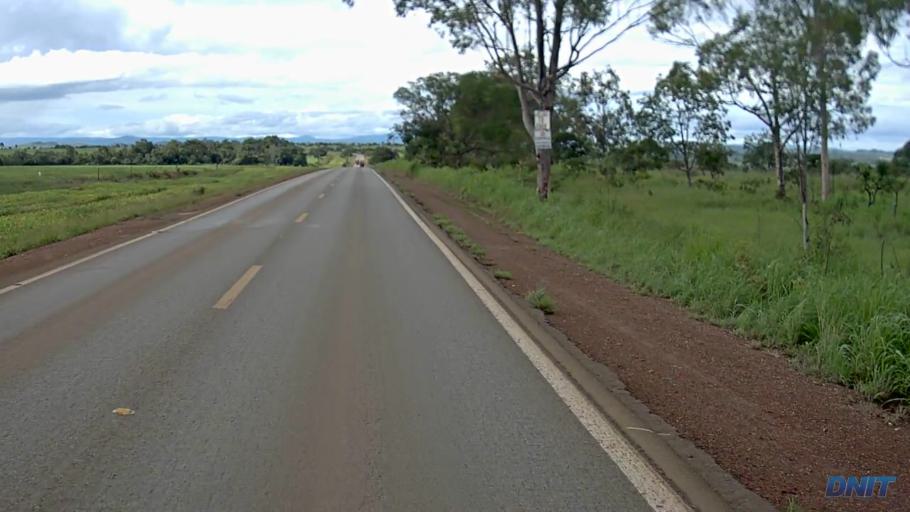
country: BR
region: Goias
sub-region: Padre Bernardo
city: Padre Bernardo
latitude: -15.3198
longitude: -48.2295
